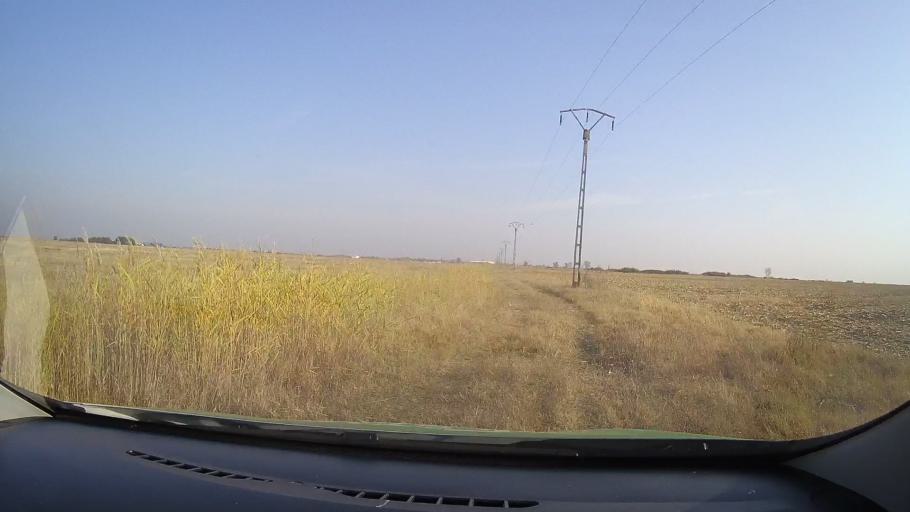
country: RO
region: Arad
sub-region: Comuna Pilu
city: Pilu
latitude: 46.5568
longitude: 21.3368
